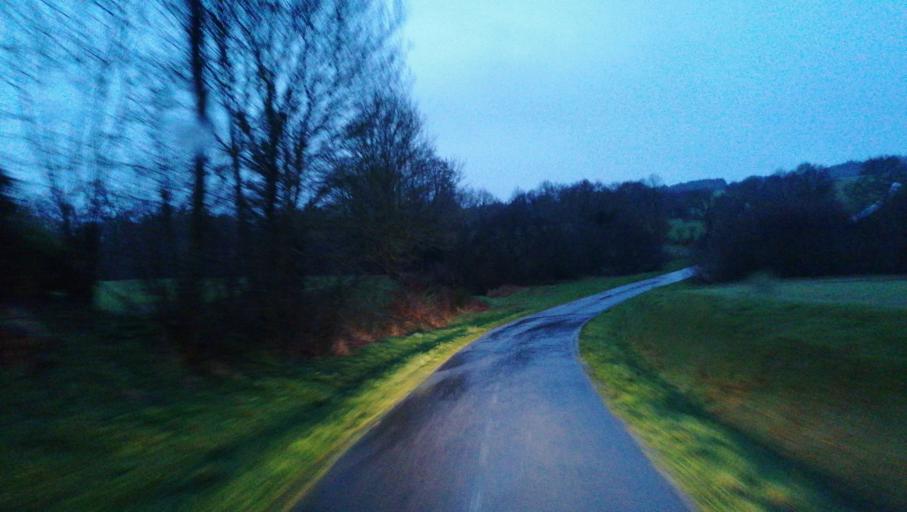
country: FR
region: Brittany
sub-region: Departement des Cotes-d'Armor
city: Plouagat
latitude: 48.4754
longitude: -2.9743
